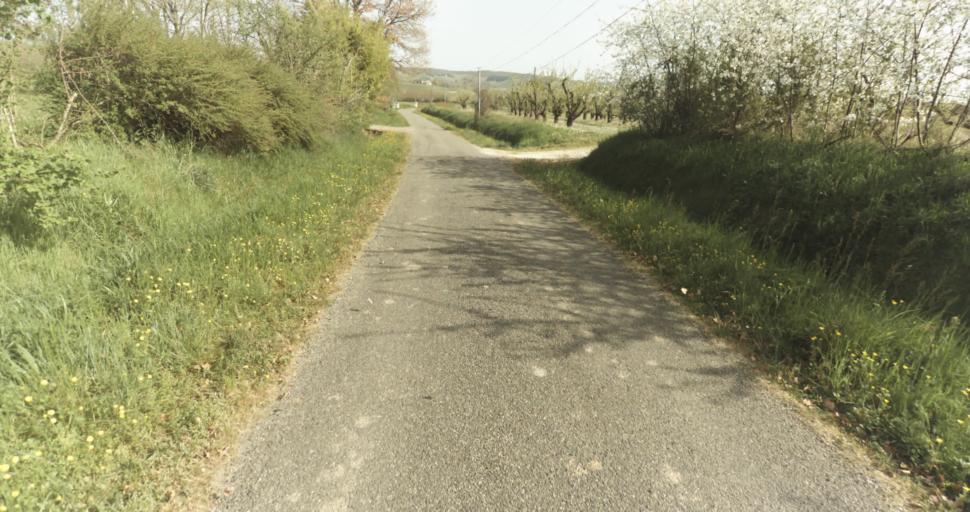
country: FR
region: Midi-Pyrenees
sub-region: Departement du Tarn-et-Garonne
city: Lafrancaise
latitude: 44.1444
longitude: 1.1712
